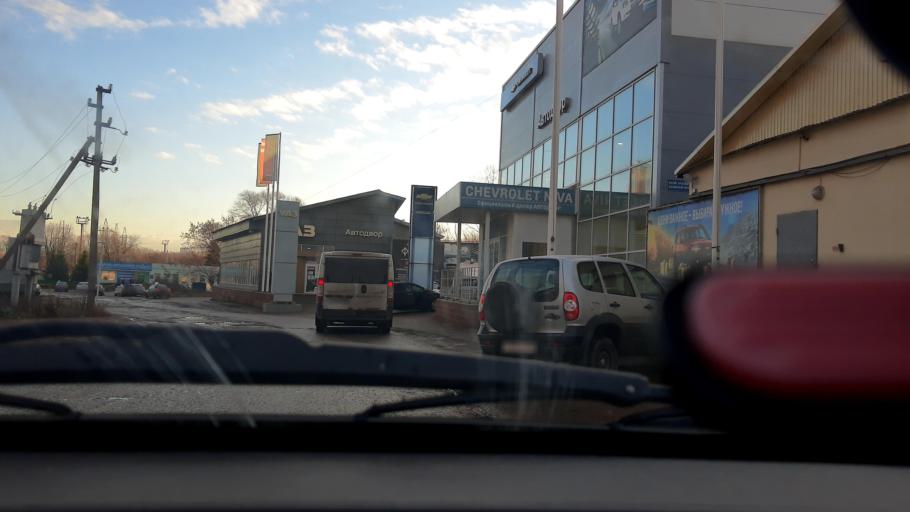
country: RU
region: Bashkortostan
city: Ufa
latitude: 54.7691
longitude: 55.9626
